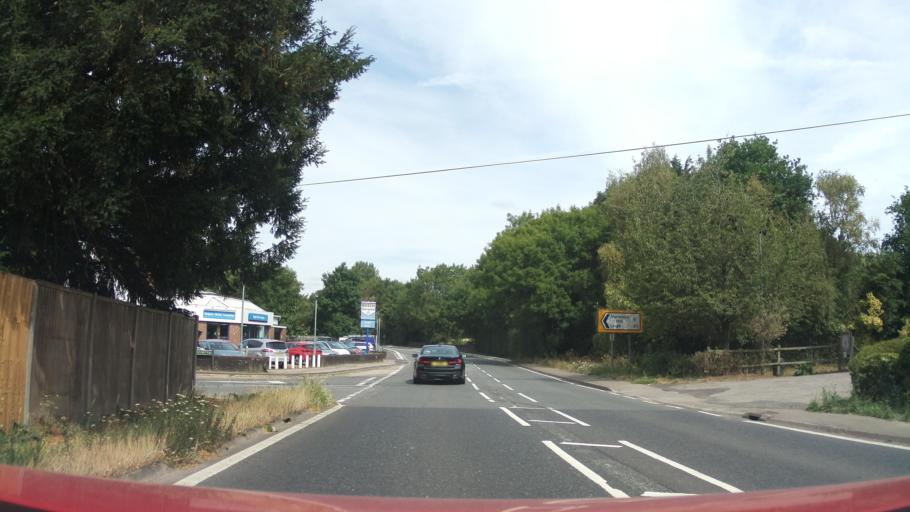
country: GB
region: England
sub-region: Surrey
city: Salfords
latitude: 51.2078
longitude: -0.1993
